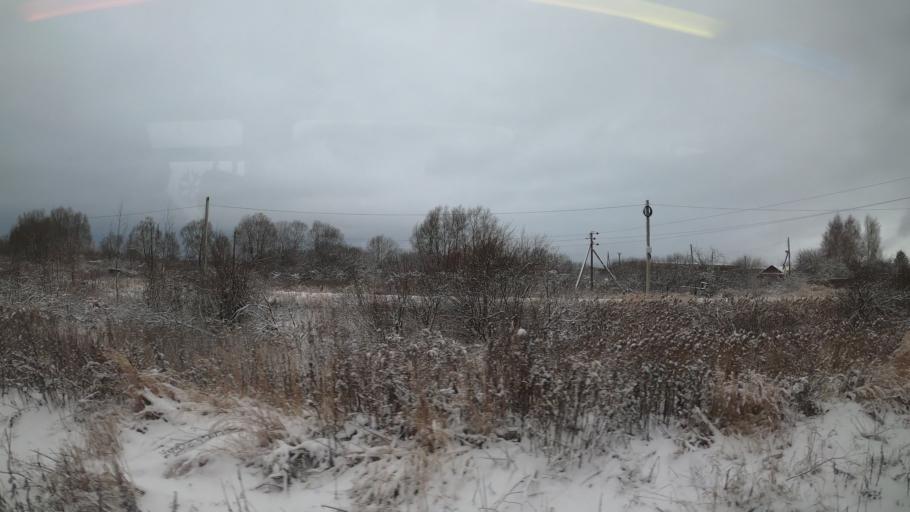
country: RU
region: Jaroslavl
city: Pereslavl'-Zalesskiy
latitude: 56.7329
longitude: 38.8981
